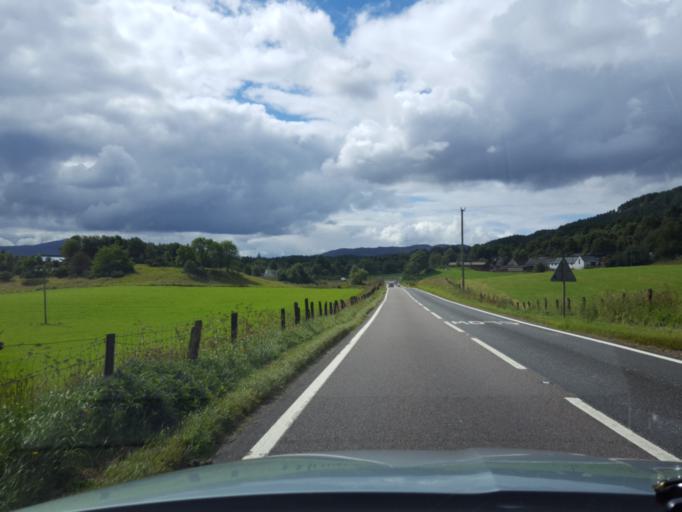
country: GB
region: Scotland
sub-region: Highland
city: Aviemore
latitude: 57.2302
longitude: -3.8131
